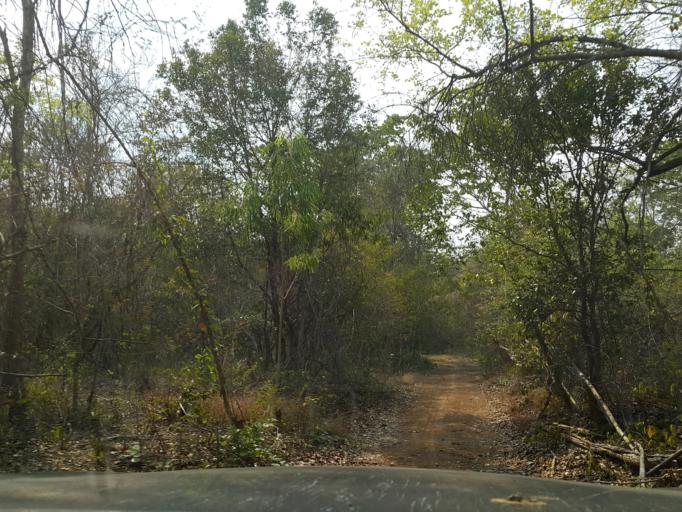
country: TH
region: Lampang
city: Mae Phrik
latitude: 17.5216
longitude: 98.9977
